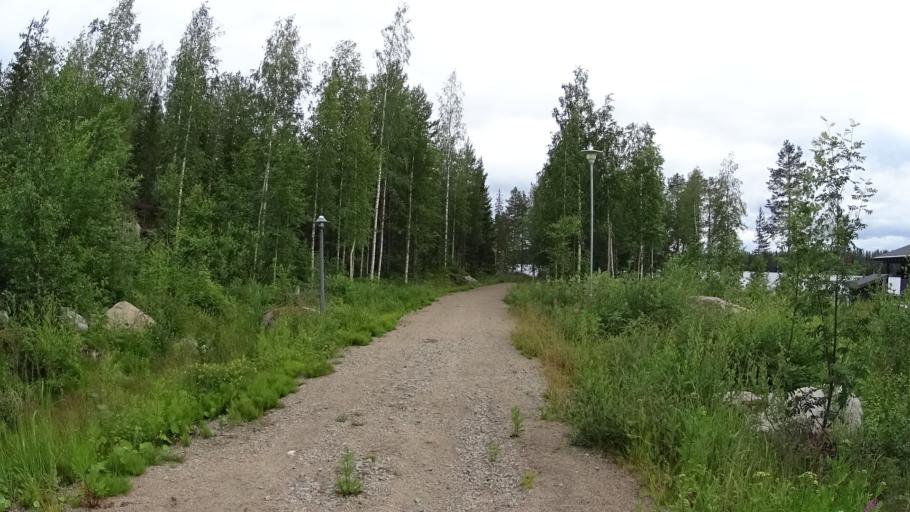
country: FI
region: Southern Ostrobothnia
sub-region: Kuusiokunnat
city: AEhtaeri
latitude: 62.5320
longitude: 24.1872
